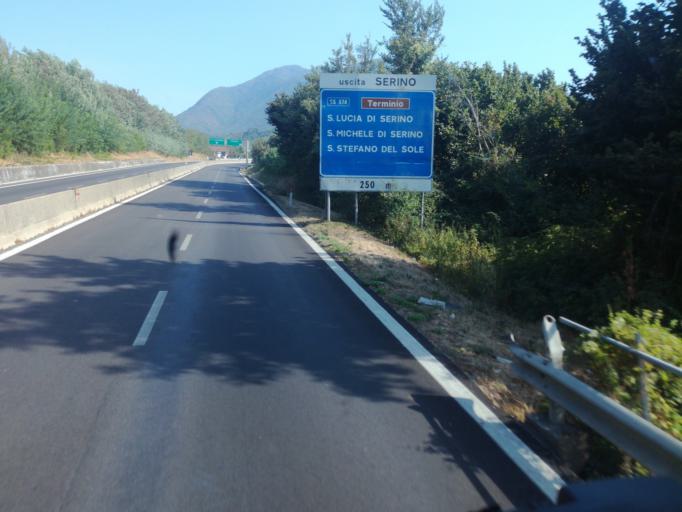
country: IT
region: Campania
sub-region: Provincia di Avellino
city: San Michele di Serino
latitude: 40.8651
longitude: 14.8583
